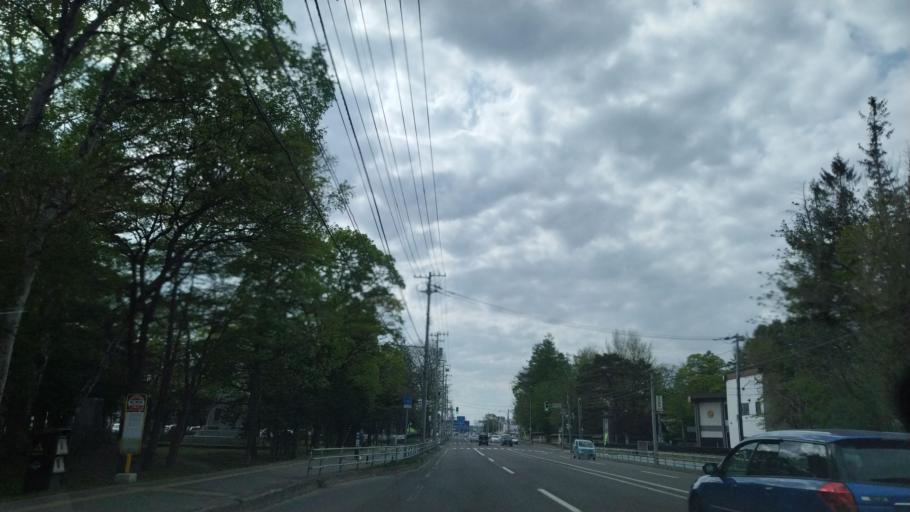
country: JP
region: Hokkaido
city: Obihiro
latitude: 42.9301
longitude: 143.2106
